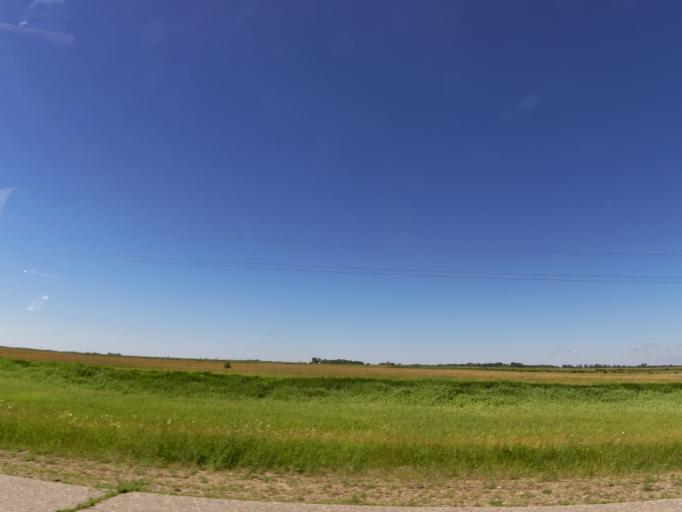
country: US
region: Minnesota
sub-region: Red Lake County
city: Red Lake Falls
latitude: 47.7465
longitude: -96.2359
